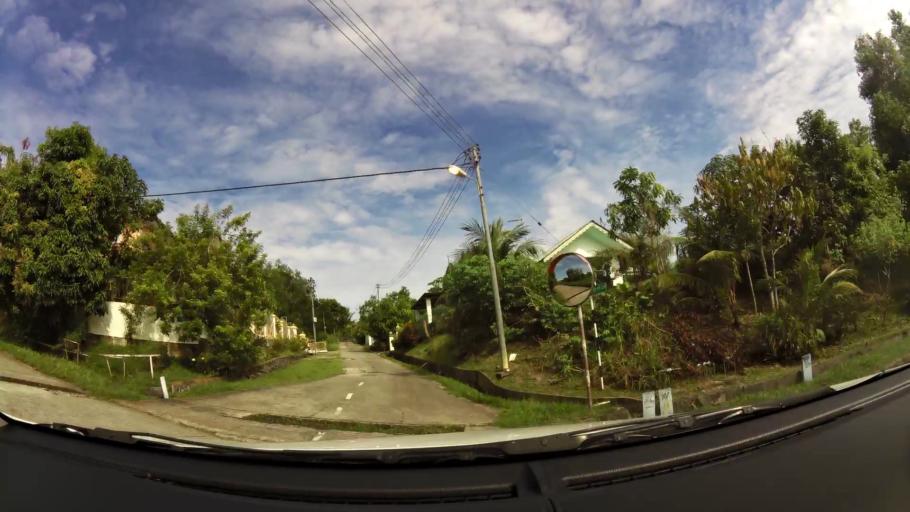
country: BN
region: Brunei and Muara
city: Bandar Seri Begawan
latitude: 4.9010
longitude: 114.9705
